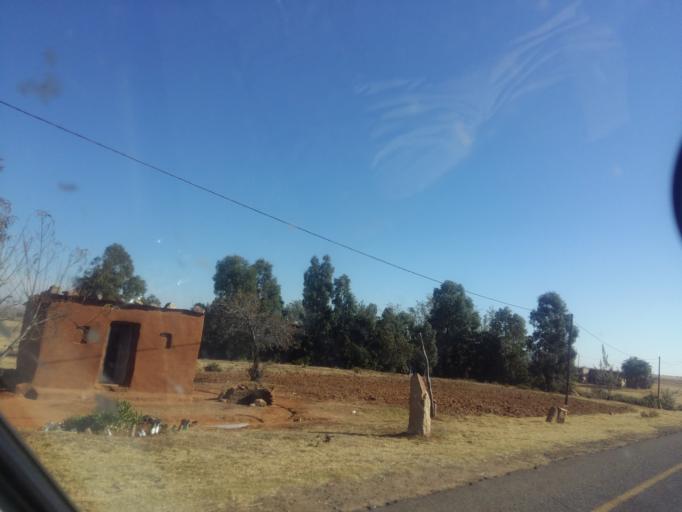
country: LS
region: Mafeteng
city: Mafeteng
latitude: -29.7735
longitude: 27.2826
